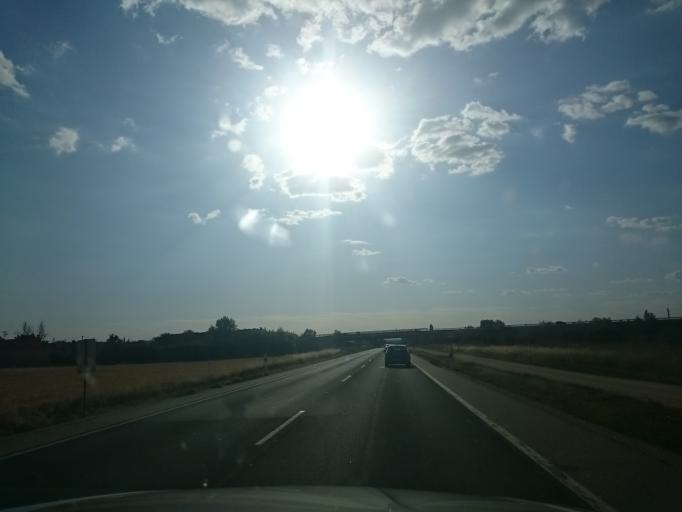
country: ES
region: Castille and Leon
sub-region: Provincia de Burgos
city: Cardenajimeno
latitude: 42.3402
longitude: -3.6053
